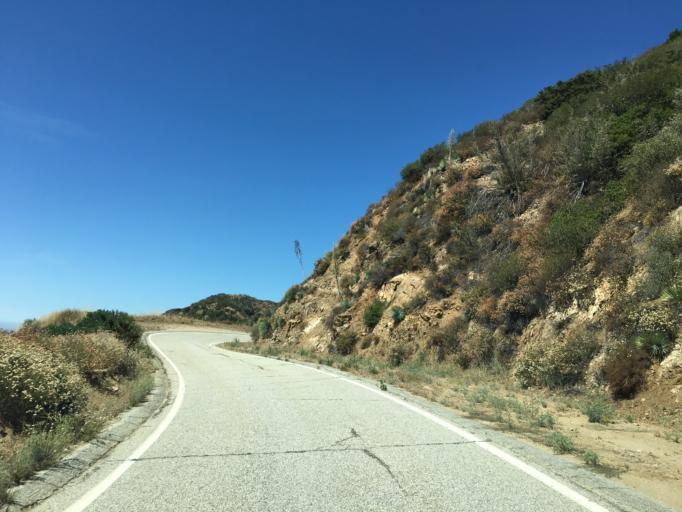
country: US
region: California
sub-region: Los Angeles County
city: Glendora
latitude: 34.2088
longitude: -117.7955
